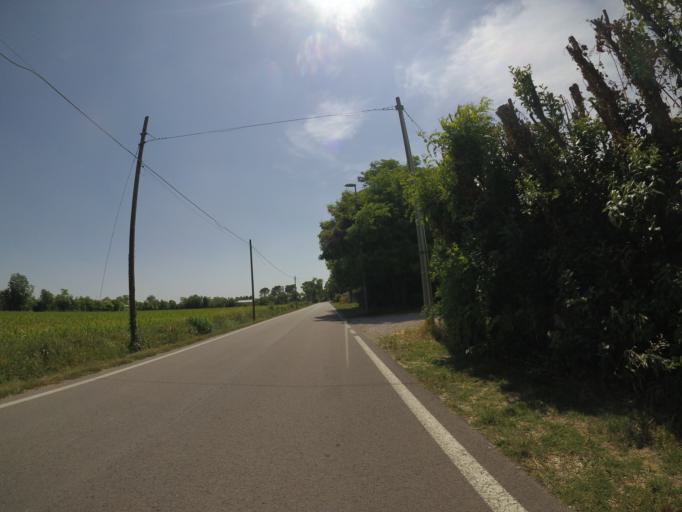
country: IT
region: Friuli Venezia Giulia
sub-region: Provincia di Udine
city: Codroipo
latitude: 45.9592
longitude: 12.9631
